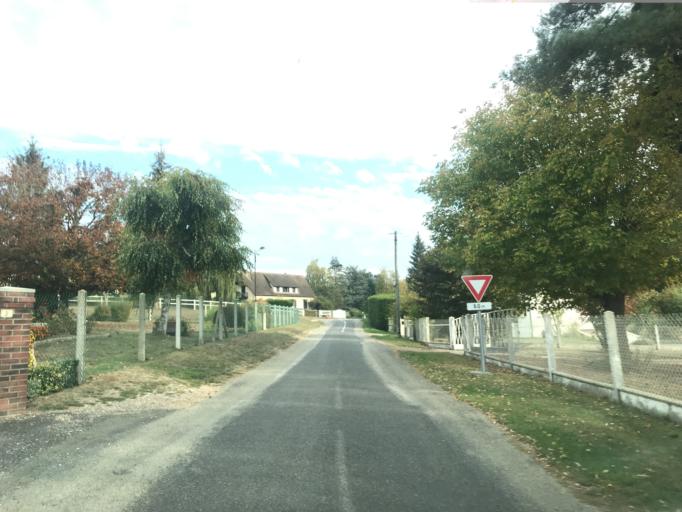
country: FR
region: Haute-Normandie
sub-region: Departement de l'Eure
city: Heudreville-sur-Eure
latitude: 49.1327
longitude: 1.2093
